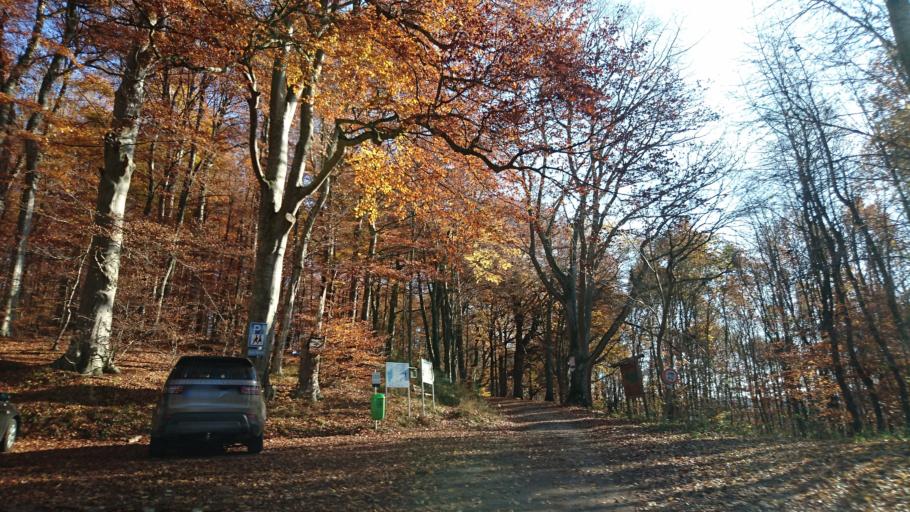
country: DE
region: Bavaria
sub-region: Swabia
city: Zusmarshausen
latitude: 48.3890
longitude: 10.5932
